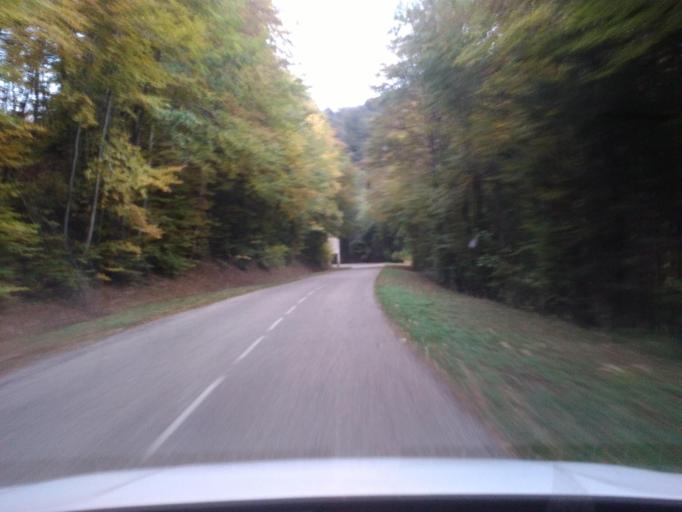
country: FR
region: Lorraine
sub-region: Departement des Vosges
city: Ban-de-Laveline
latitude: 48.3636
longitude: 7.1048
